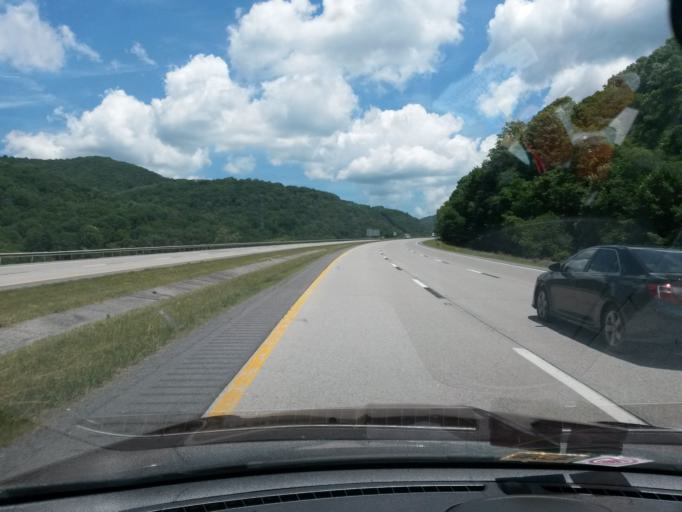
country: US
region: West Virginia
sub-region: Greenbrier County
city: Rainelle
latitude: 37.8295
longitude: -80.7976
